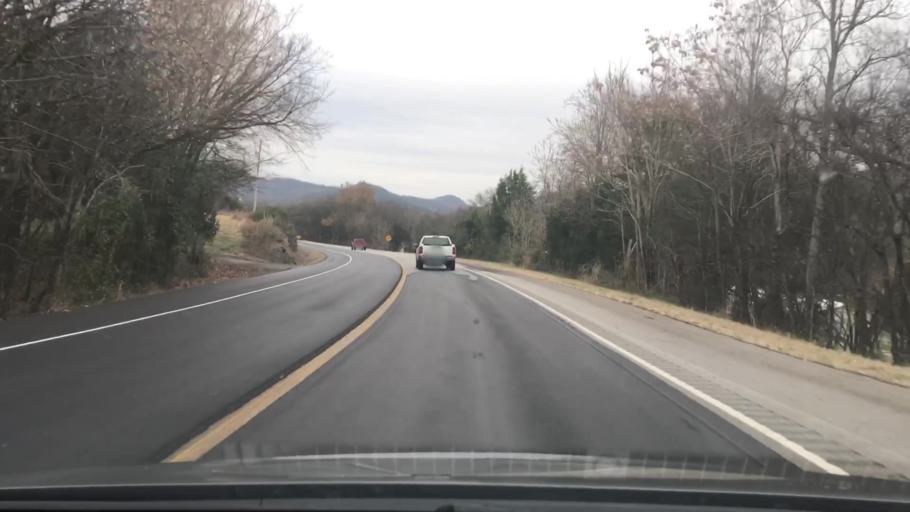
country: US
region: Tennessee
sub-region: Smith County
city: Carthage
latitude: 36.3248
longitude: -86.0210
